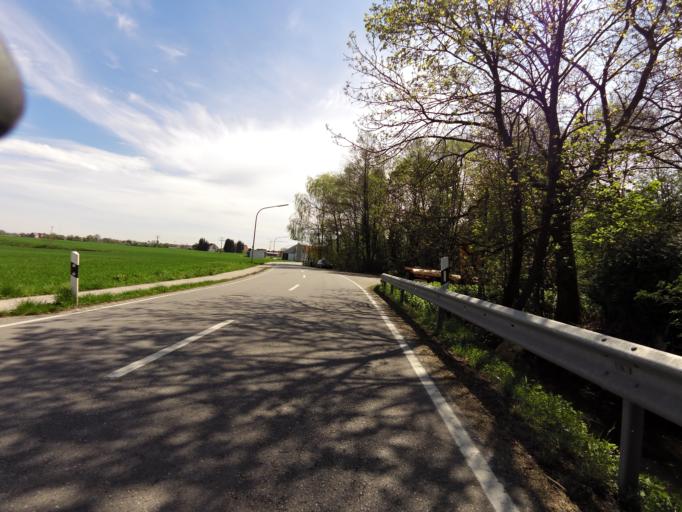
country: DE
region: Bavaria
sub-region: Lower Bavaria
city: Bruckberg
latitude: 48.5136
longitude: 12.0005
